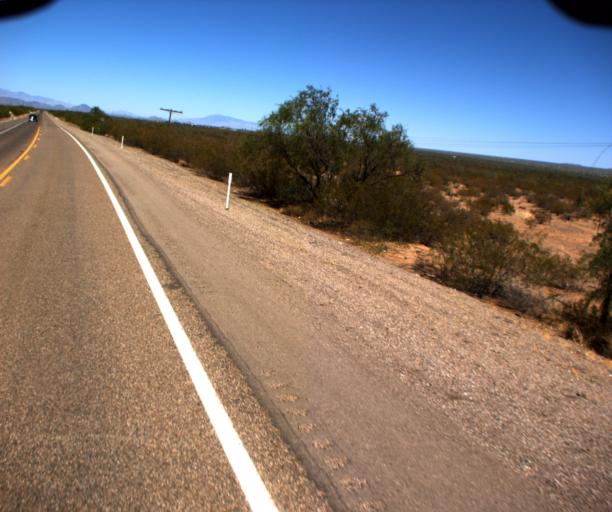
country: US
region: Arizona
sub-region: Pima County
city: Three Points
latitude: 32.0671
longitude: -111.3650
